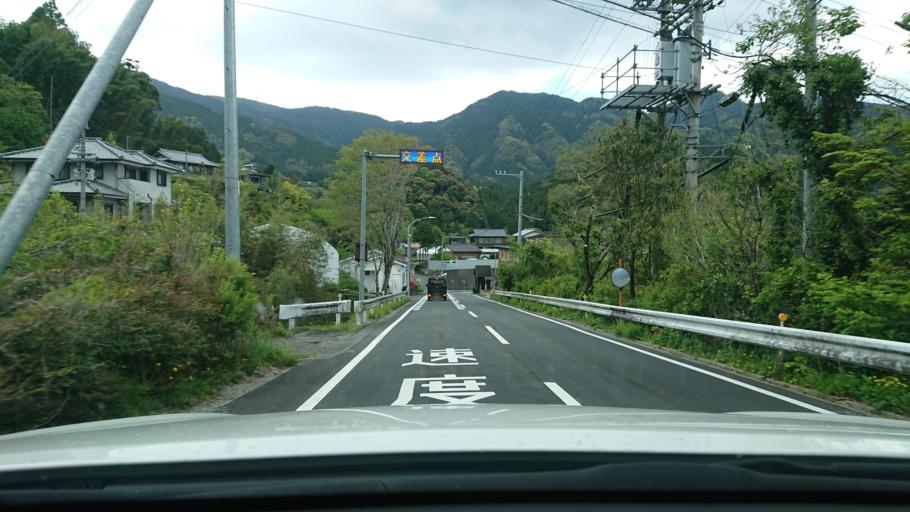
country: JP
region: Tokushima
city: Ishii
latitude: 33.9195
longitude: 134.4262
